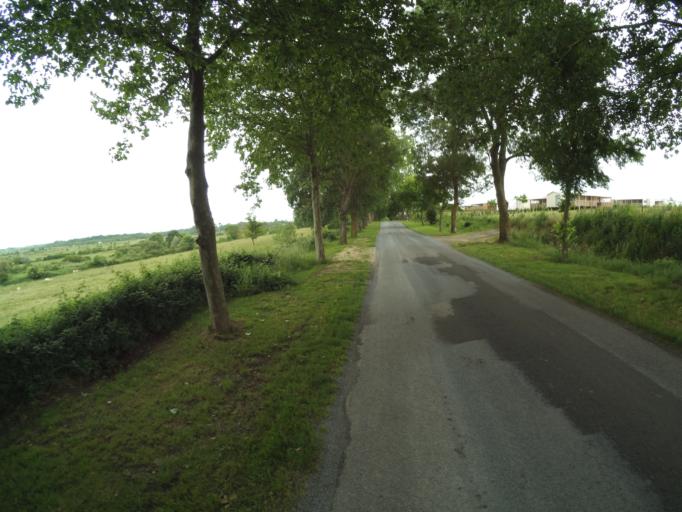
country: FR
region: Poitou-Charentes
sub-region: Departement de la Charente-Maritime
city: Saint-Laurent-de-la-Pree
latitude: 45.9885
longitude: -1.0158
